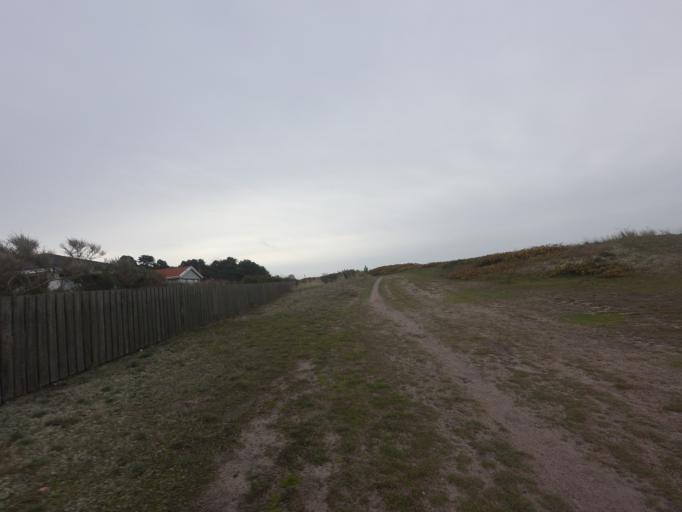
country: DK
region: Capital Region
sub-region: Helsingor Kommune
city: Hellebaek
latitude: 56.1284
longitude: 12.5941
